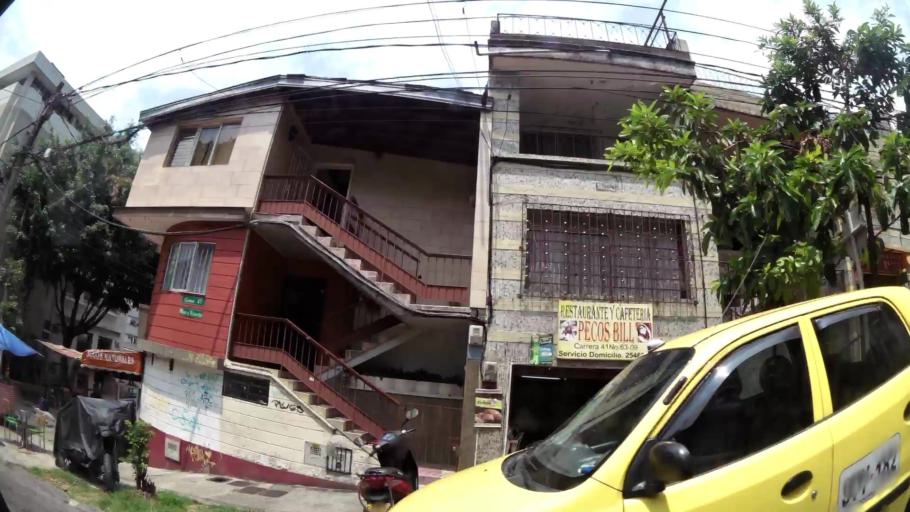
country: CO
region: Antioquia
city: Medellin
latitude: 6.2557
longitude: -75.5558
